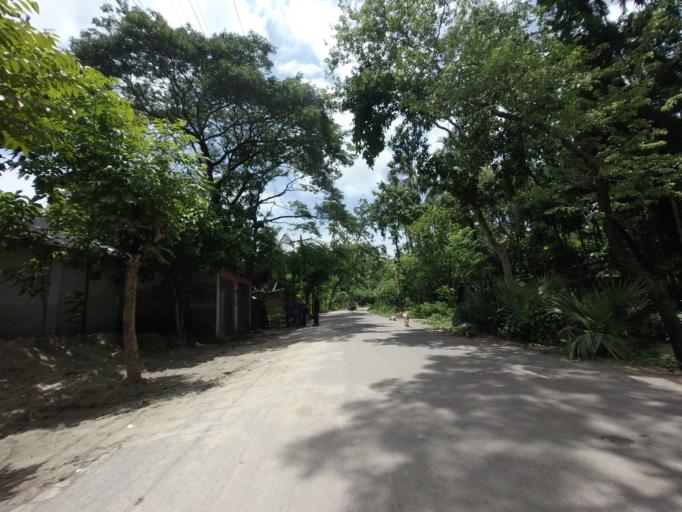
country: BD
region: Khulna
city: Kalia
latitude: 23.0334
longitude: 89.6325
